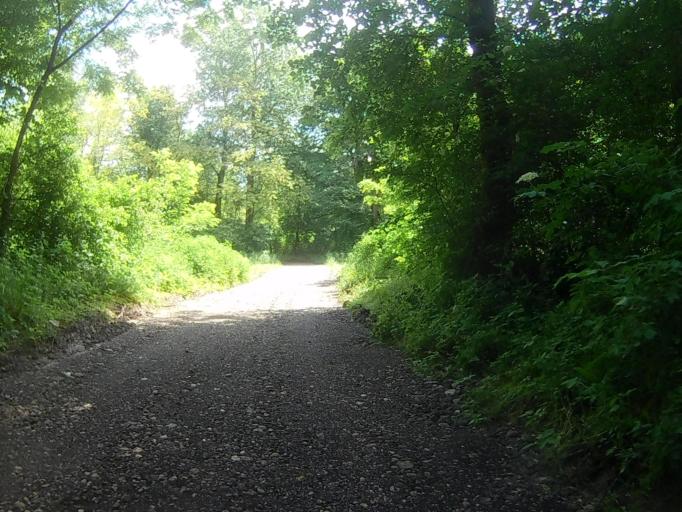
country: SI
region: Starse
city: Starse
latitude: 46.4817
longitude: 15.7562
